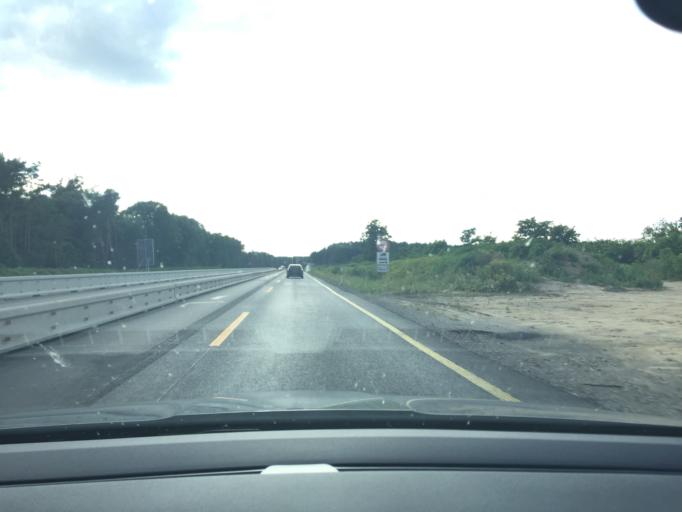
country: DE
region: Brandenburg
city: Storkow
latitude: 52.3126
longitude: 13.9342
